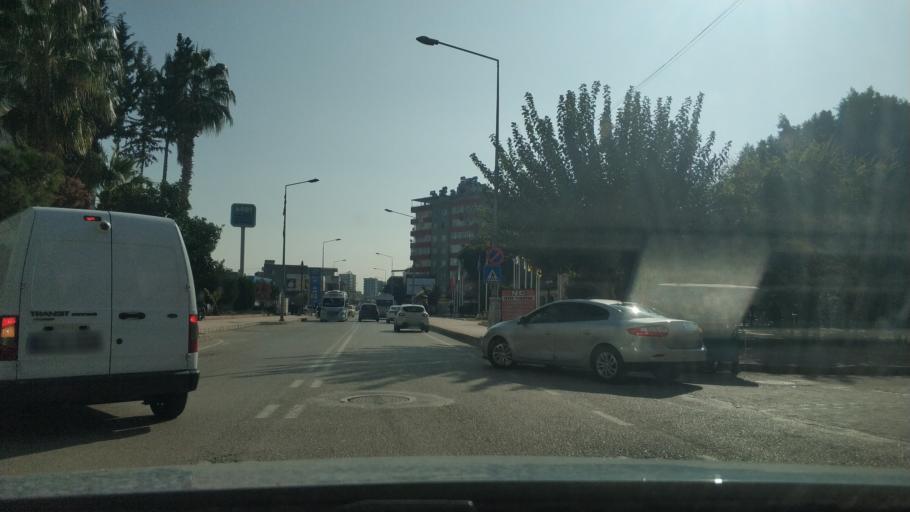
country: TR
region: Adana
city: Seyhan
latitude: 37.0213
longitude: 35.2938
